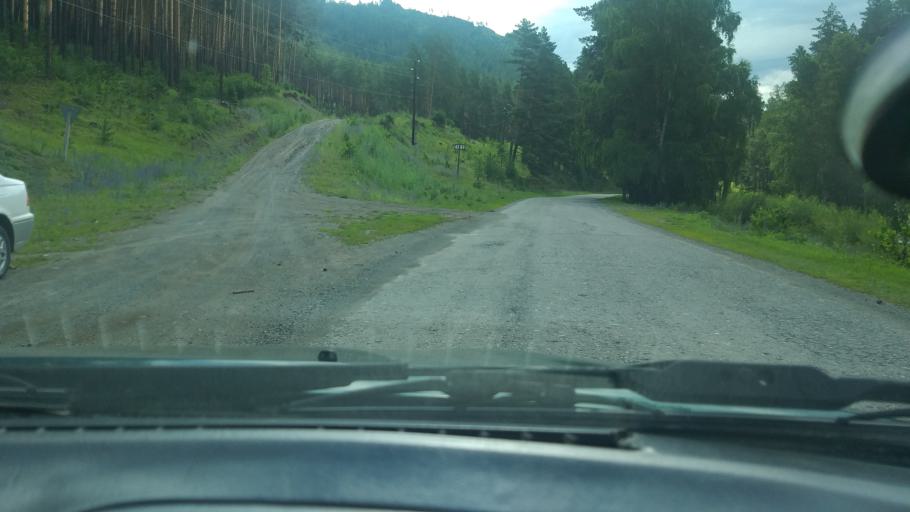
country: RU
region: Altay
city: Chemal
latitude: 51.3910
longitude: 86.0483
